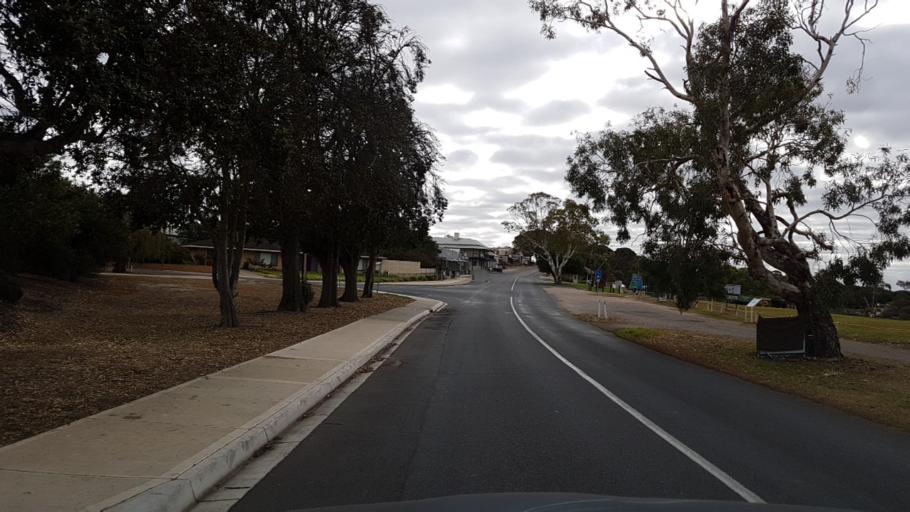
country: AU
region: South Australia
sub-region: Alexandrina
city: Langhorne Creek
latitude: -35.4087
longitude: 138.9714
